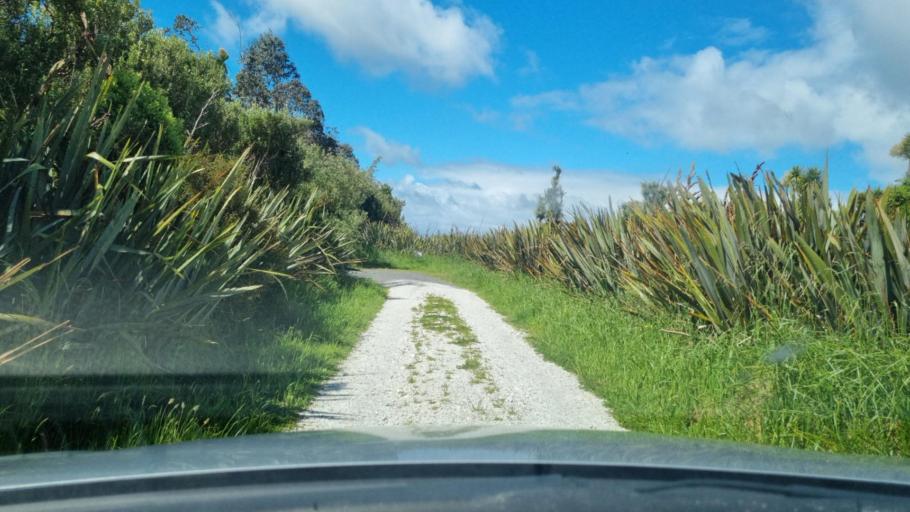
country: NZ
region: Southland
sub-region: Invercargill City
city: Invercargill
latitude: -46.4529
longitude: 168.3167
